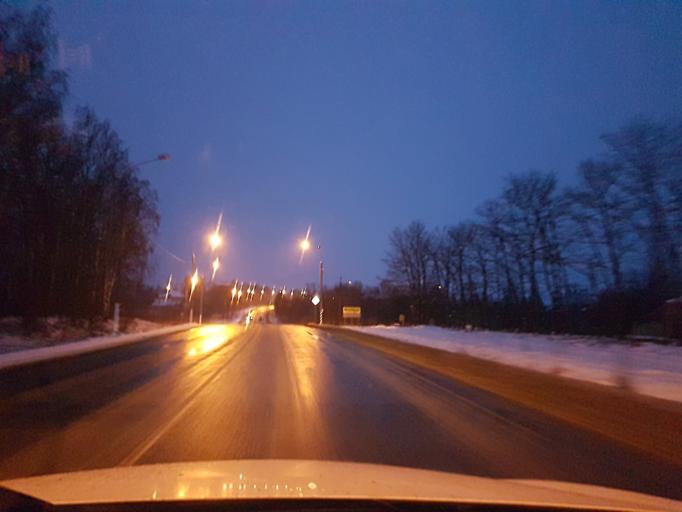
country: RU
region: Tverskaya
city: Novozavidovskiy
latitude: 56.5689
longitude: 36.4401
